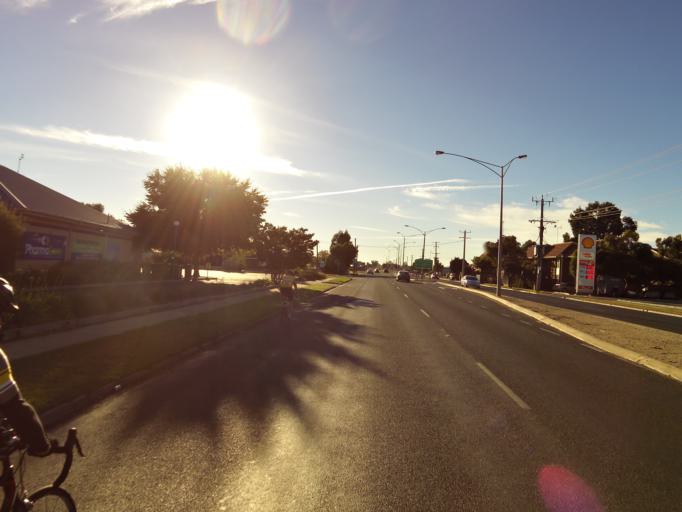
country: AU
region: Victoria
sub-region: Campaspe
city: Echuca
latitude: -36.1404
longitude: 144.7485
